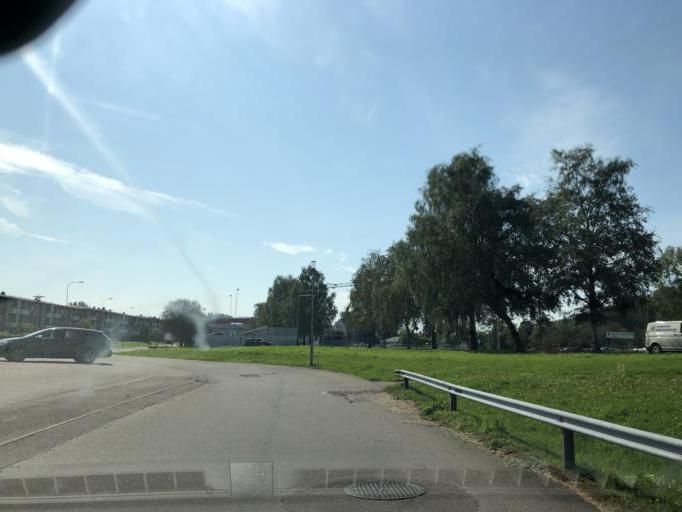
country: SE
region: Vaestra Goetaland
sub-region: Goteborg
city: Goeteborg
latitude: 57.7540
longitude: 11.9813
